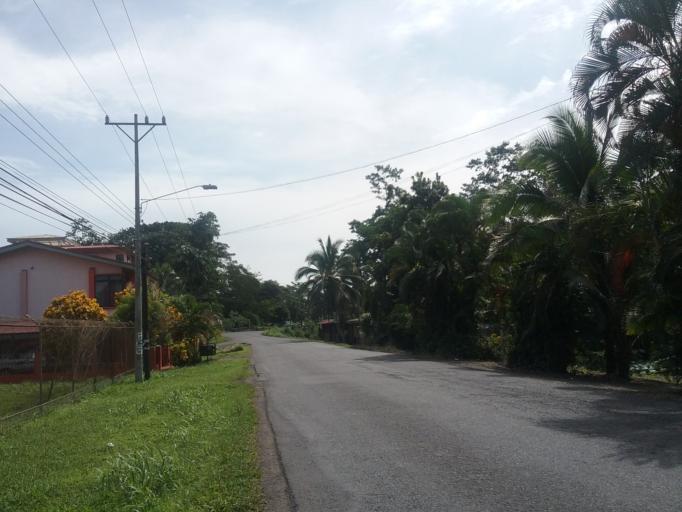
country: CR
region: Limon
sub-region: Canton de Pococi
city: Guapiles
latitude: 10.3204
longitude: -83.9112
